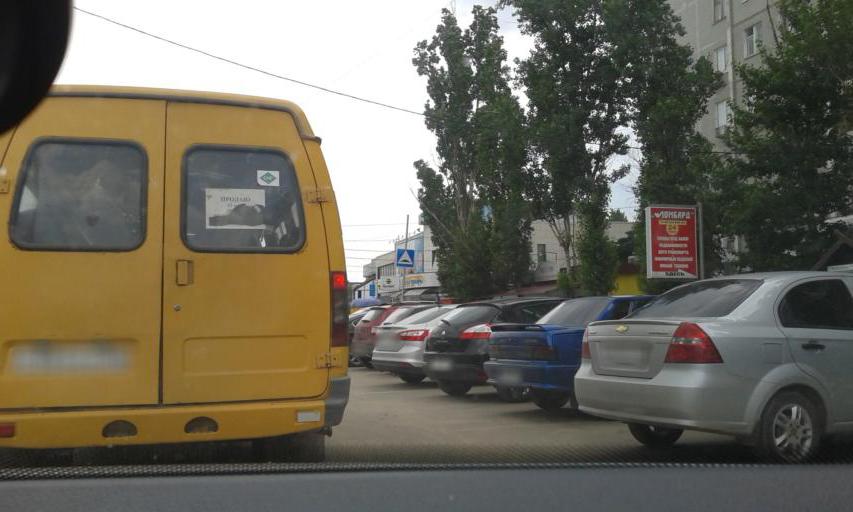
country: RU
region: Volgograd
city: Volgograd
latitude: 48.7571
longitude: 44.5018
